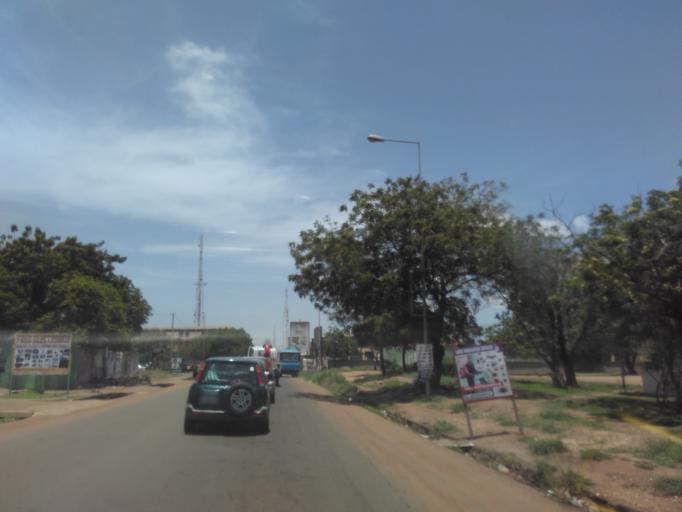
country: GH
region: Greater Accra
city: Tema
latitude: 5.6818
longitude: -0.0161
